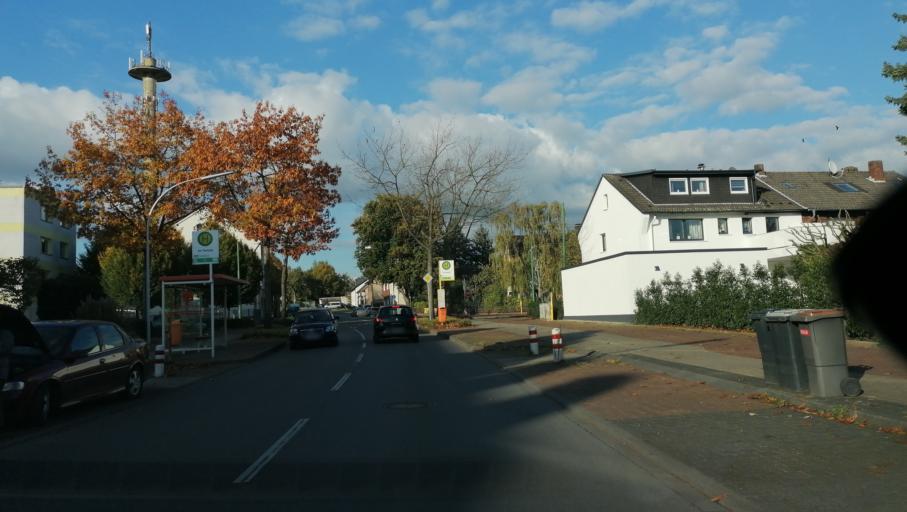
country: DE
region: North Rhine-Westphalia
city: Datteln
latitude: 51.6562
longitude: 7.3315
